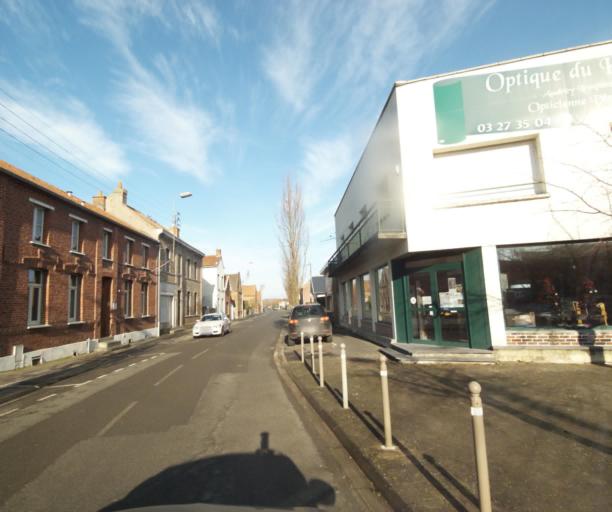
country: FR
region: Nord-Pas-de-Calais
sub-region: Departement du Nord
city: Maing
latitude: 50.3099
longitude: 3.4845
